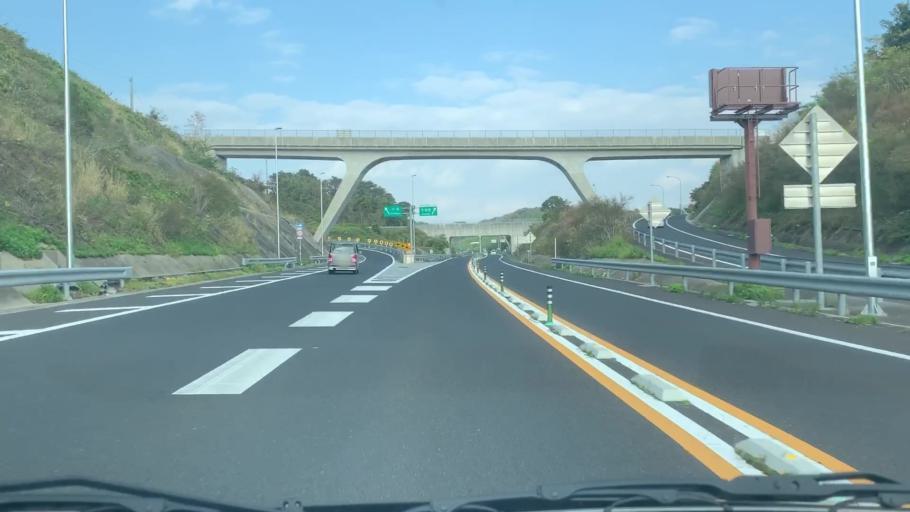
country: JP
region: Nagasaki
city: Sasebo
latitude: 33.0425
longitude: 129.7470
